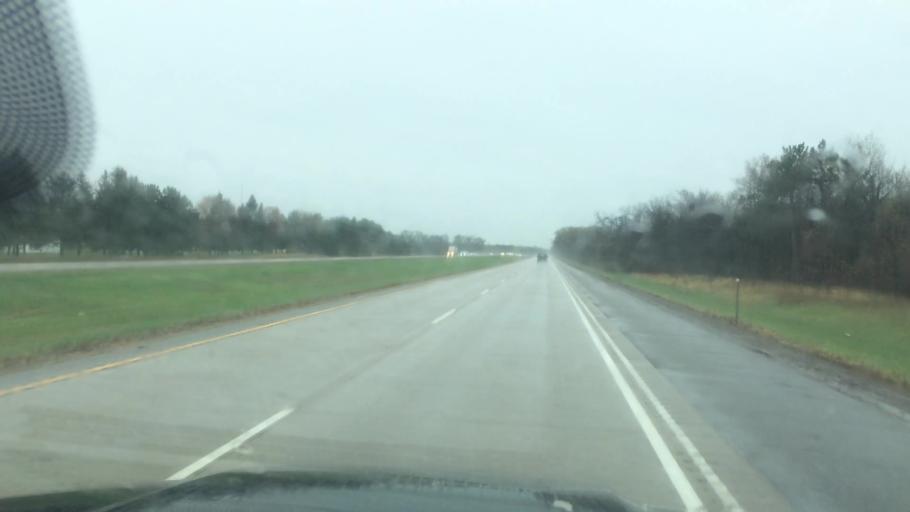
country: US
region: Wisconsin
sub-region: Marathon County
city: Mosinee
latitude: 44.6570
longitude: -89.6416
